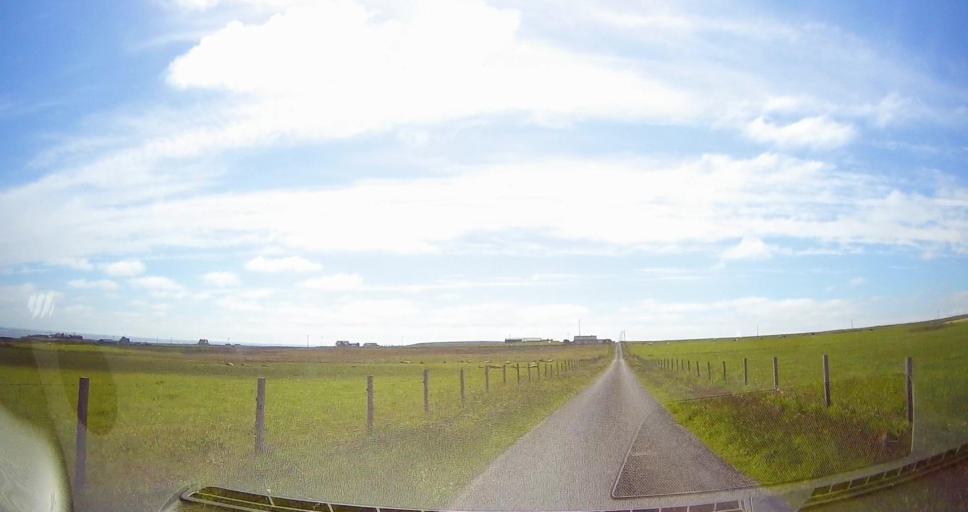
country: GB
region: Scotland
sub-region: Orkney Islands
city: Kirkwall
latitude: 58.8349
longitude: -2.9010
